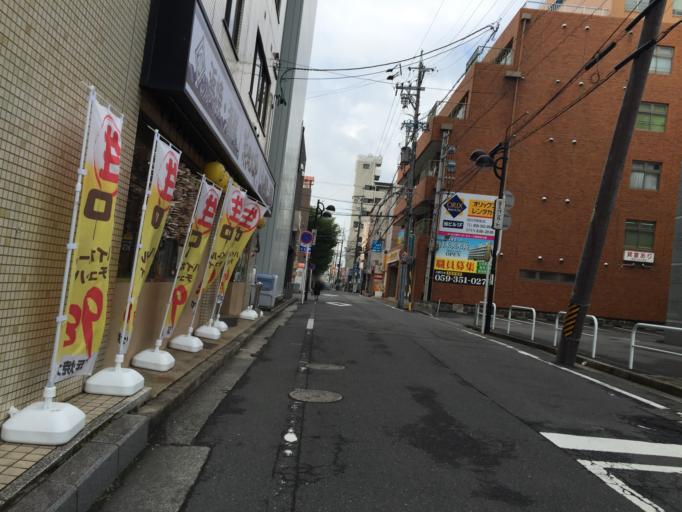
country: JP
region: Mie
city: Yokkaichi
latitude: 34.9665
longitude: 136.6164
